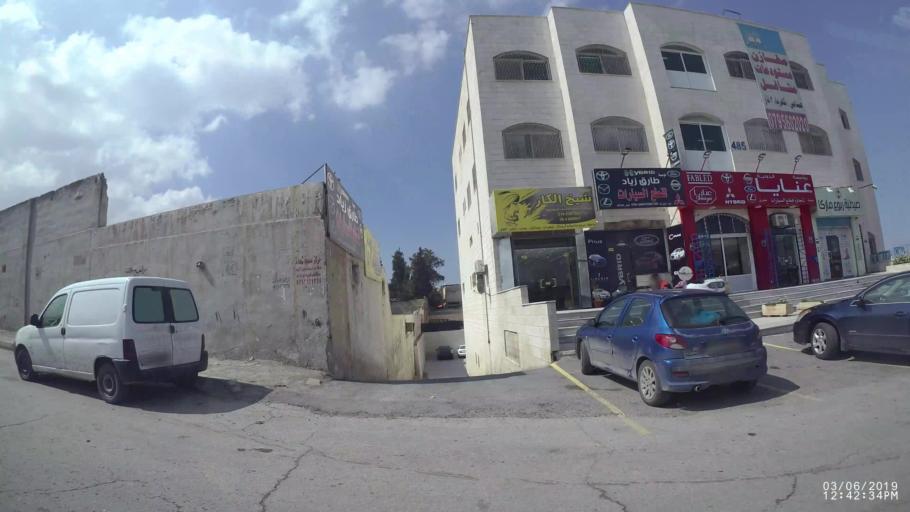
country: JO
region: Zarqa
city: Russeifa
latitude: 31.9896
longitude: 36.0013
